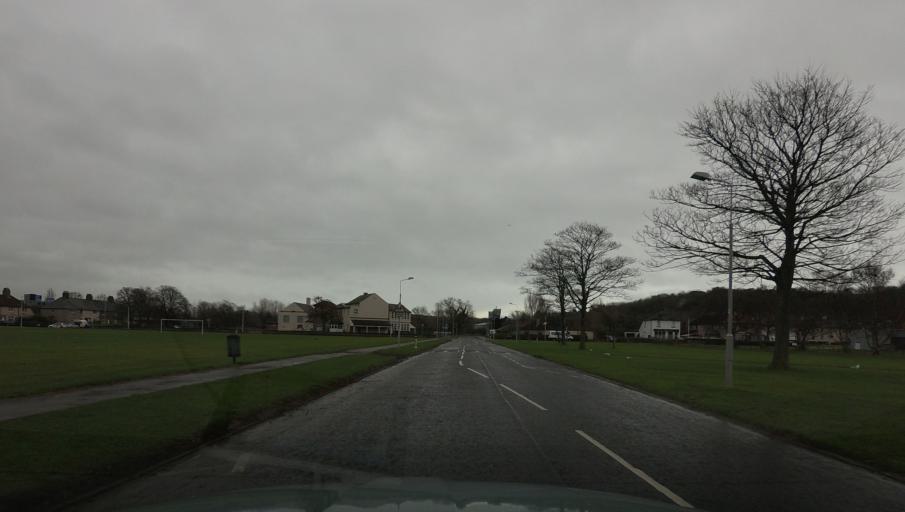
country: GB
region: Scotland
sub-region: Fife
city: Inverkeithing
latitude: 56.0394
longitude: -3.4116
